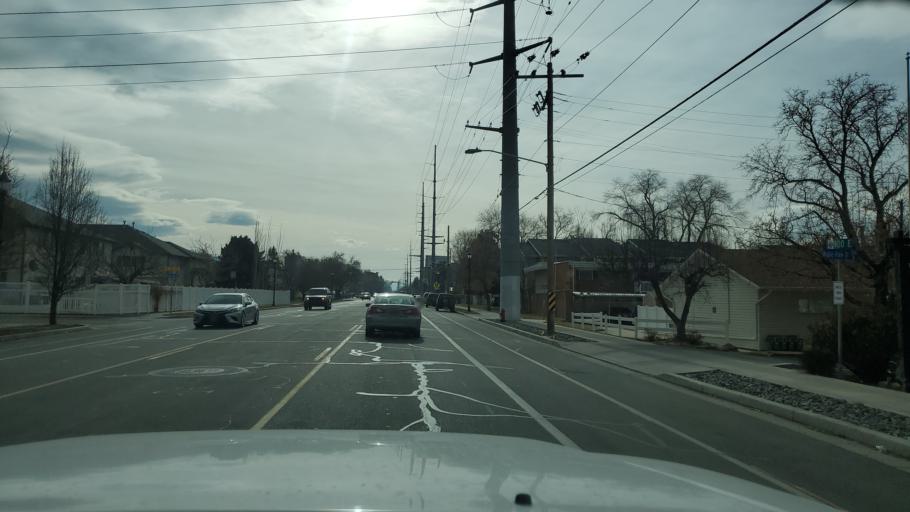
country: US
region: Utah
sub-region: Salt Lake County
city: Millcreek
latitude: 40.6896
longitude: -111.8656
